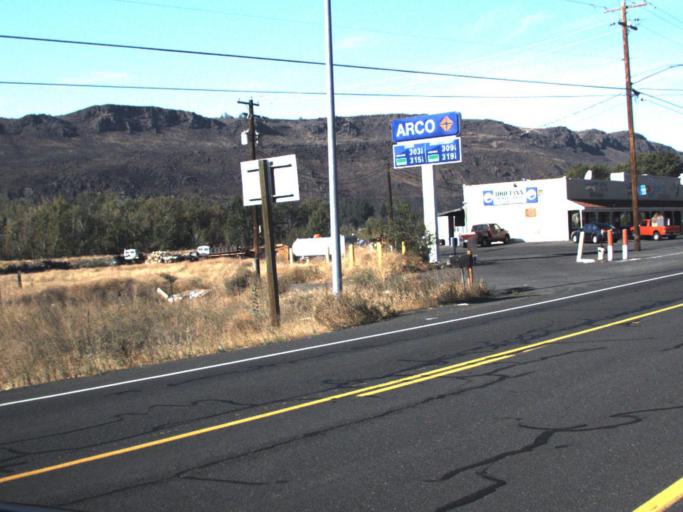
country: US
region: Washington
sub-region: Yakima County
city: Tieton
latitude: 46.7299
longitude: -120.7062
